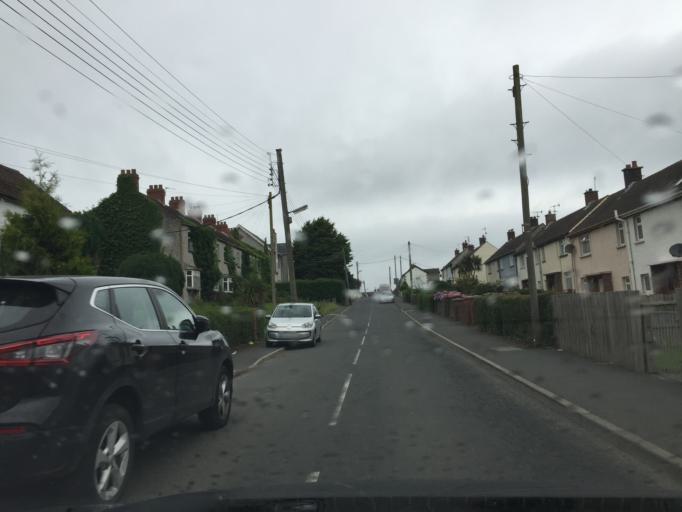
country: GB
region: Northern Ireland
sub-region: Down District
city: Kircubbin
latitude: 54.4880
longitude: -5.5302
